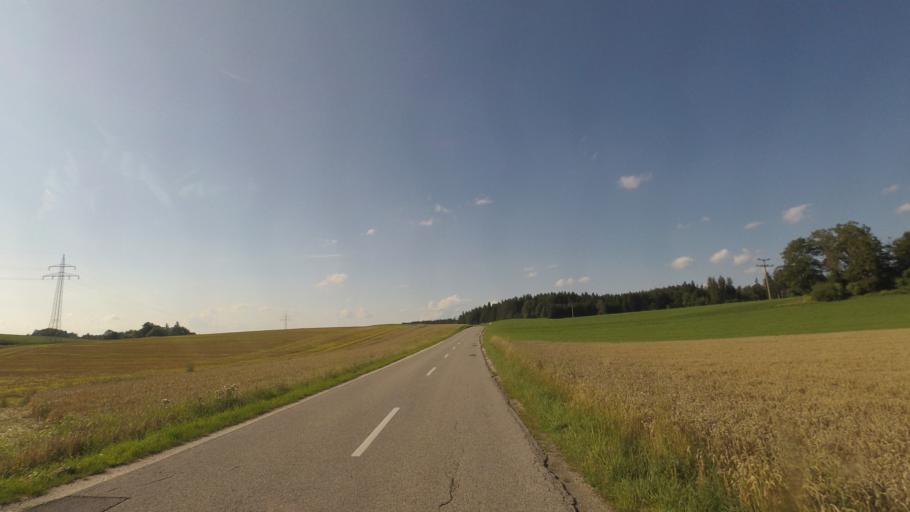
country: DE
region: Bavaria
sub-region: Upper Bavaria
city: Nussdorf
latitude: 47.8843
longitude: 12.6172
